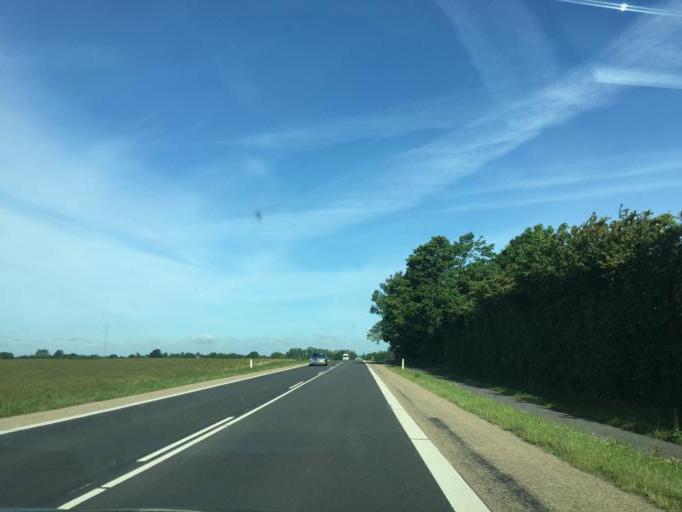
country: DK
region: South Denmark
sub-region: Middelfart Kommune
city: Norre Aby
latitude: 55.4758
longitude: 9.8657
